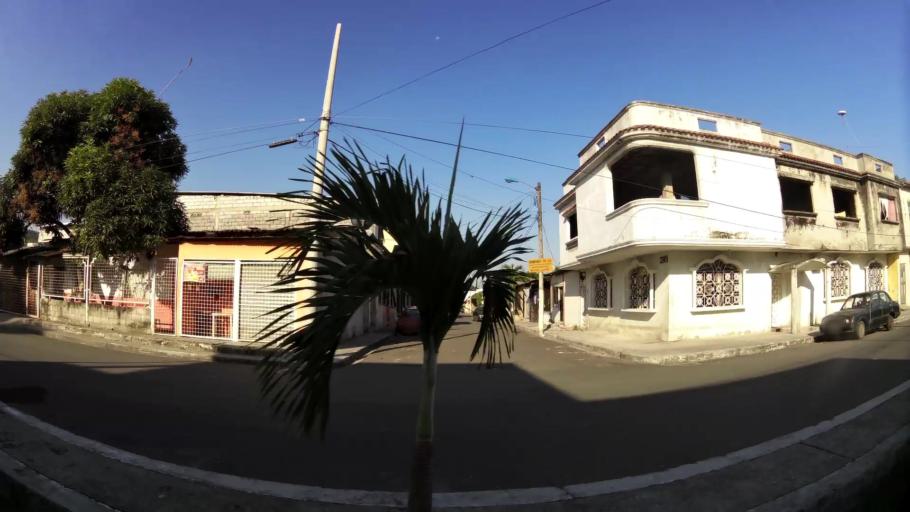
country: EC
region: Guayas
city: Santa Lucia
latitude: -2.1921
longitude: -79.9615
